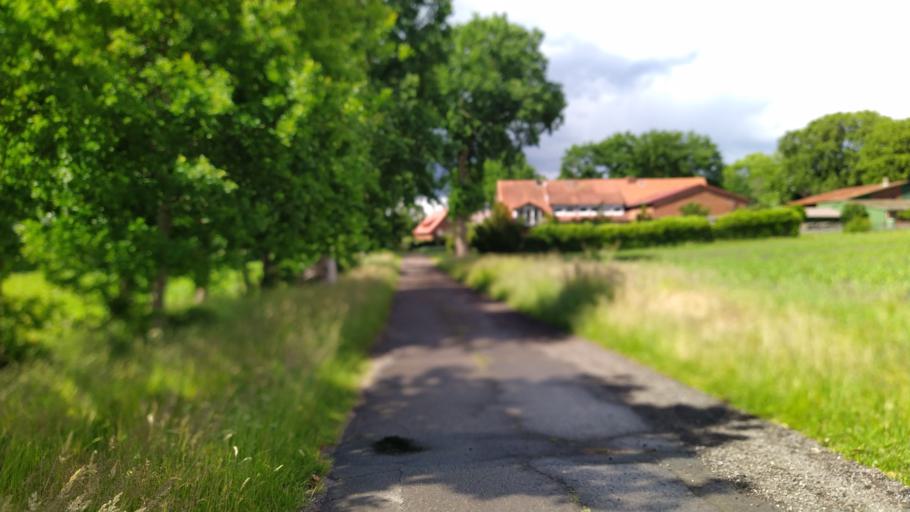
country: DE
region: Lower Saxony
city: Deinstedt
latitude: 53.4424
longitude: 9.2587
